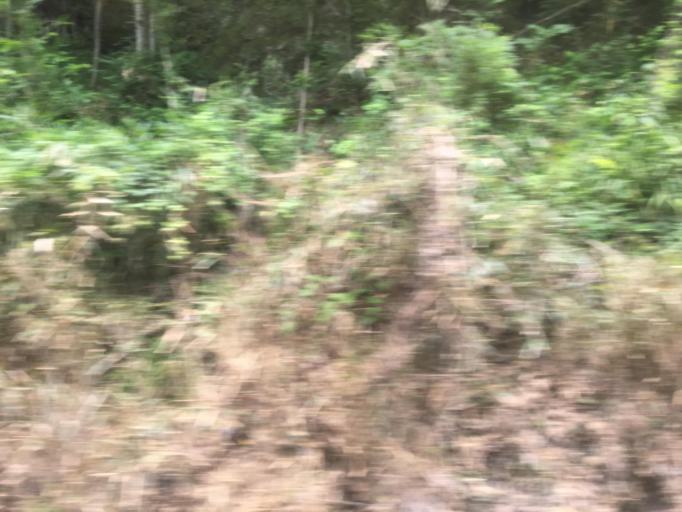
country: JP
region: Gunma
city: Tomioka
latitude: 36.2267
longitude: 138.7940
